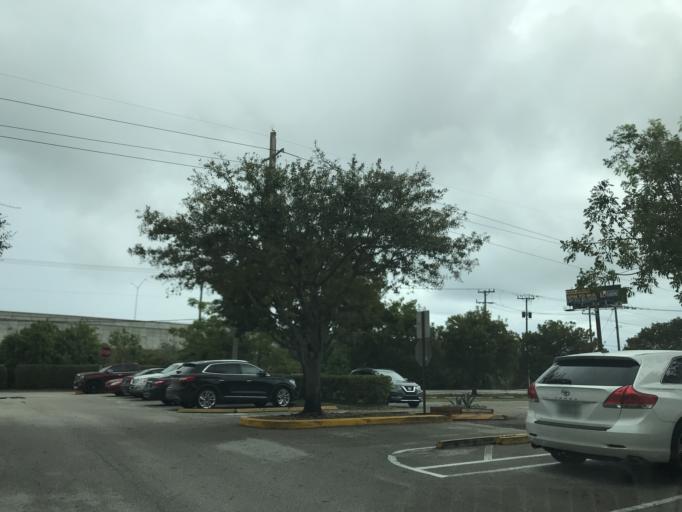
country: US
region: Florida
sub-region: Palm Beach County
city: Delray Beach
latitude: 26.4708
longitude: -80.0907
